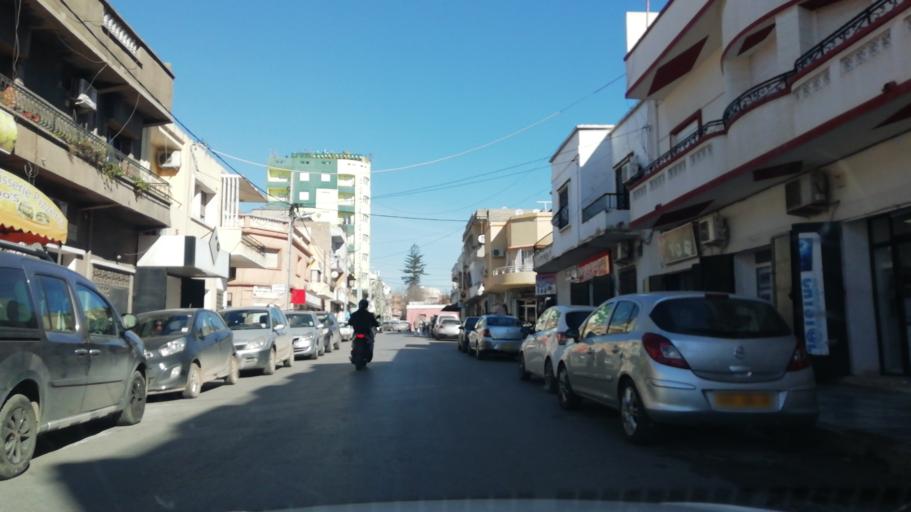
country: DZ
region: Oran
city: Oran
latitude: 35.6955
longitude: -0.6215
